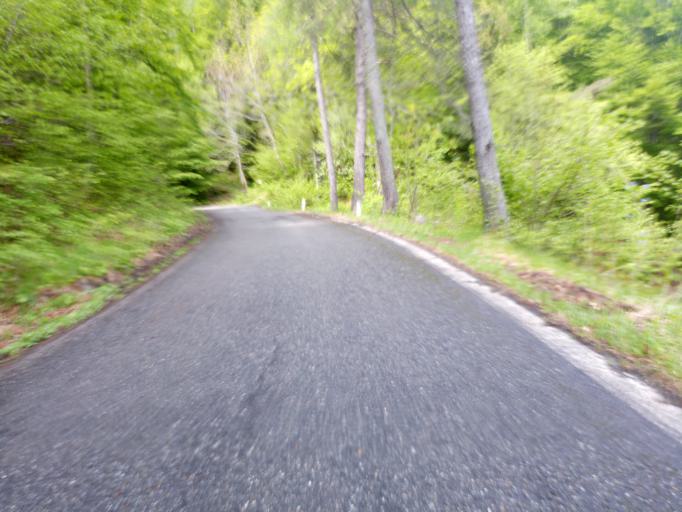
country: IT
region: Piedmont
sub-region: Provincia di Torino
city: Meana di Susa
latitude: 45.1065
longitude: 7.0616
